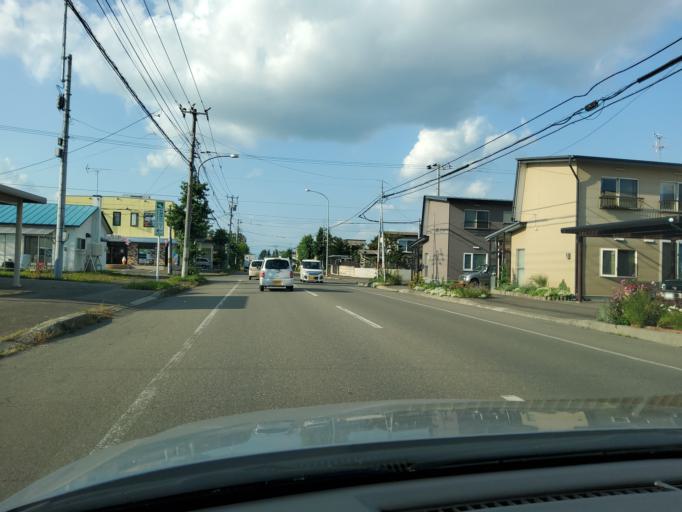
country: JP
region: Hokkaido
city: Obihiro
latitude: 42.9068
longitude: 143.1732
